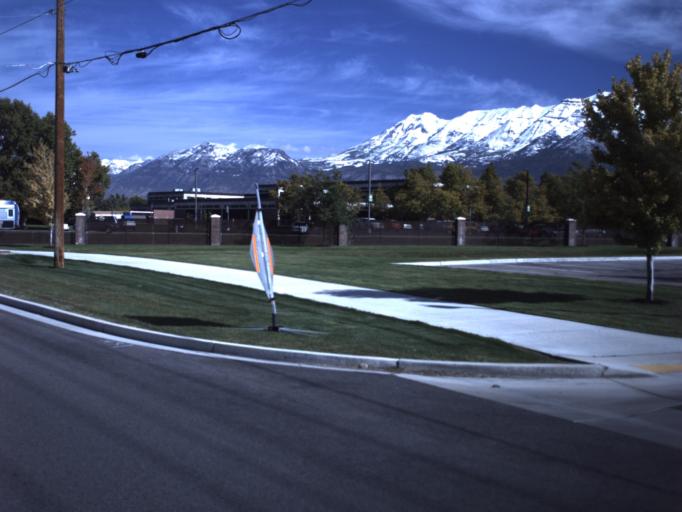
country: US
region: Utah
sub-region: Utah County
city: Orem
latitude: 40.2783
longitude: -111.7298
